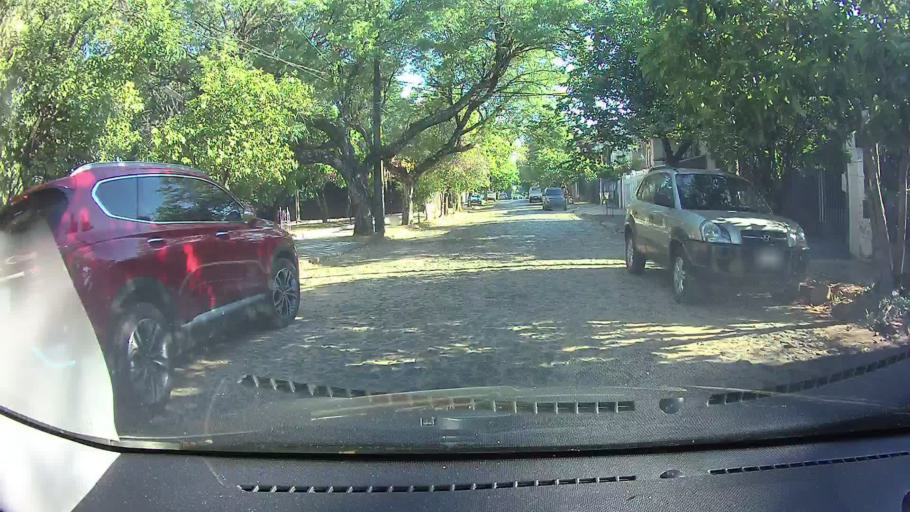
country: PY
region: Asuncion
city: Asuncion
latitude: -25.2832
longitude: -57.5992
